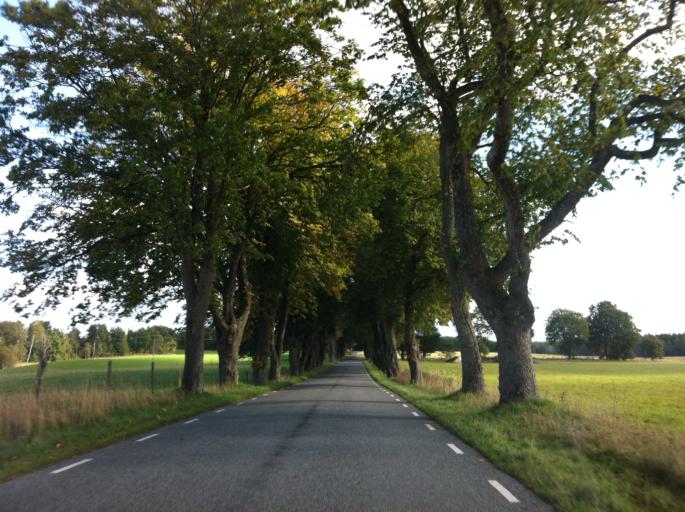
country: SE
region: Skane
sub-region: Kristianstads Kommun
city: Degeberga
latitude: 55.7139
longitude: 13.9694
